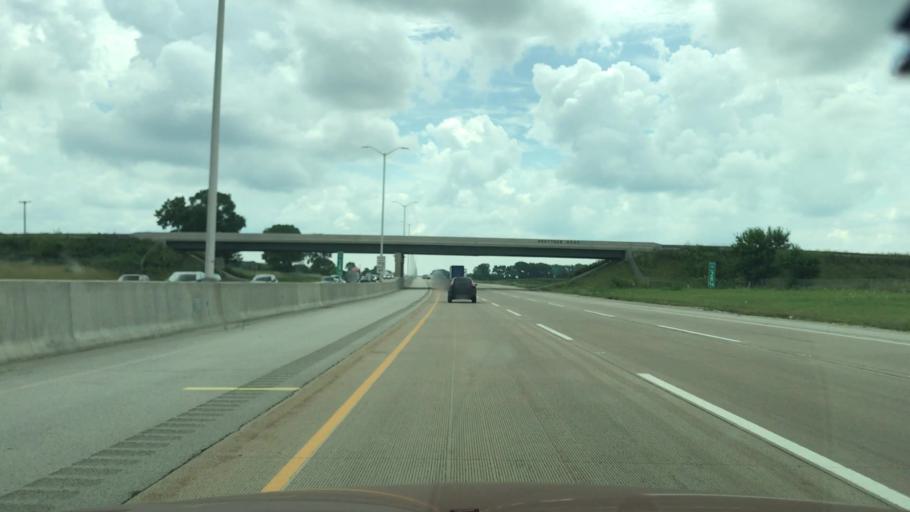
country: US
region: Illinois
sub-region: Boone County
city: Belvidere
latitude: 42.2199
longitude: -88.7508
